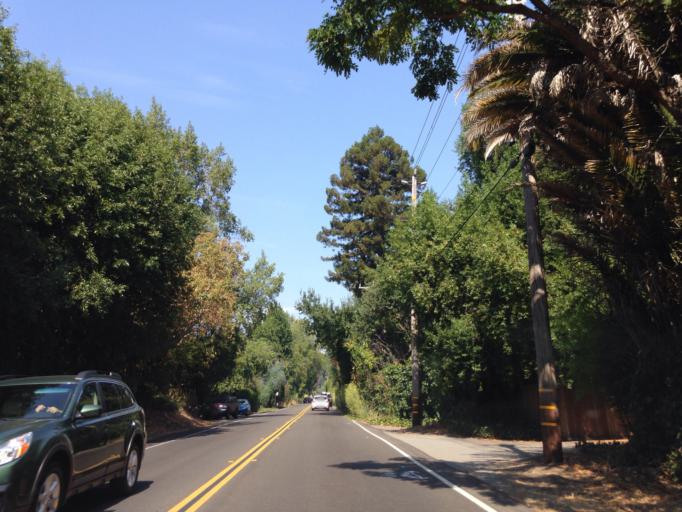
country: US
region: California
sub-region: Marin County
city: San Anselmo
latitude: 37.9802
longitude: -122.5733
